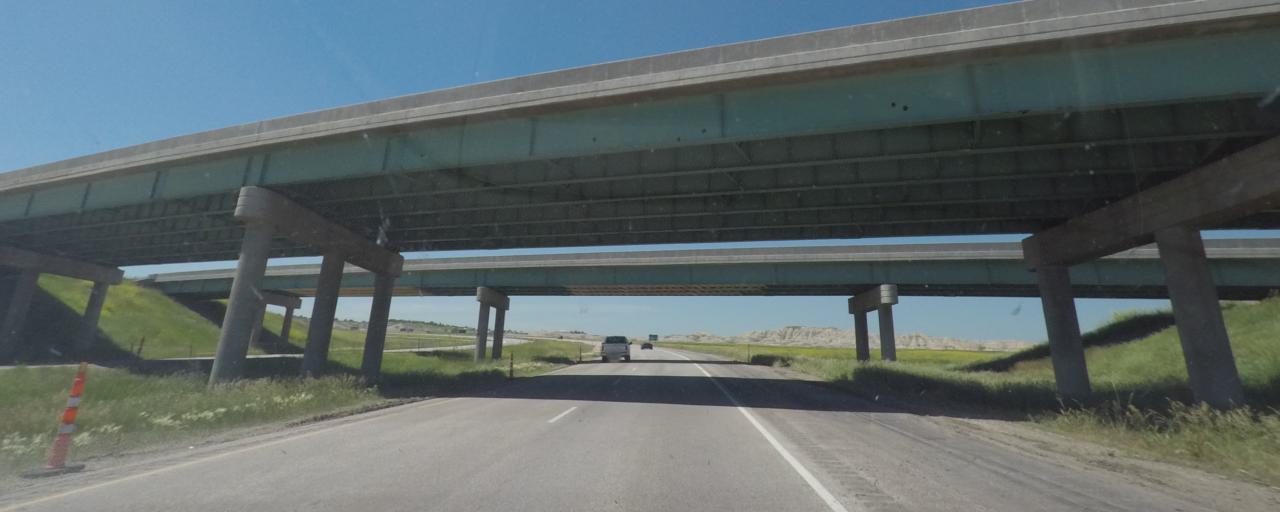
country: US
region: South Dakota
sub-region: Haakon County
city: Philip
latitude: 43.9849
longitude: -102.2068
